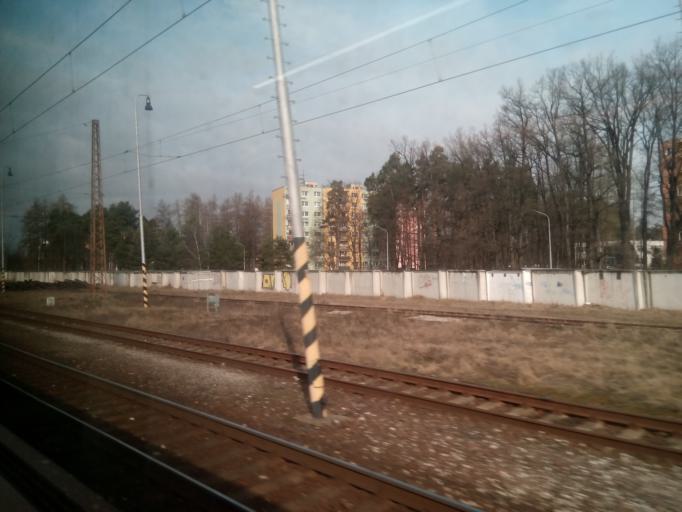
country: SK
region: Zilinsky
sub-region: Okres Zilina
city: Liptovsky Hradok
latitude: 49.0382
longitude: 19.7200
